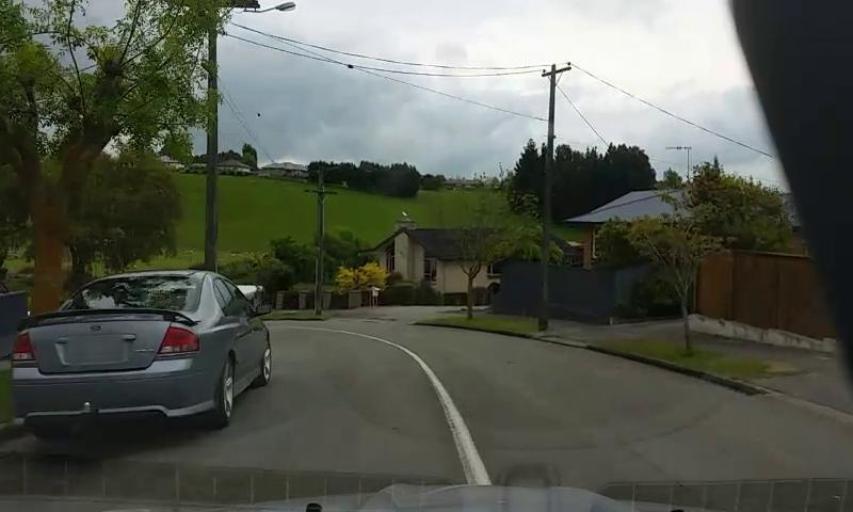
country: NZ
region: Canterbury
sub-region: Timaru District
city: Timaru
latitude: -44.3738
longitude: 171.2346
